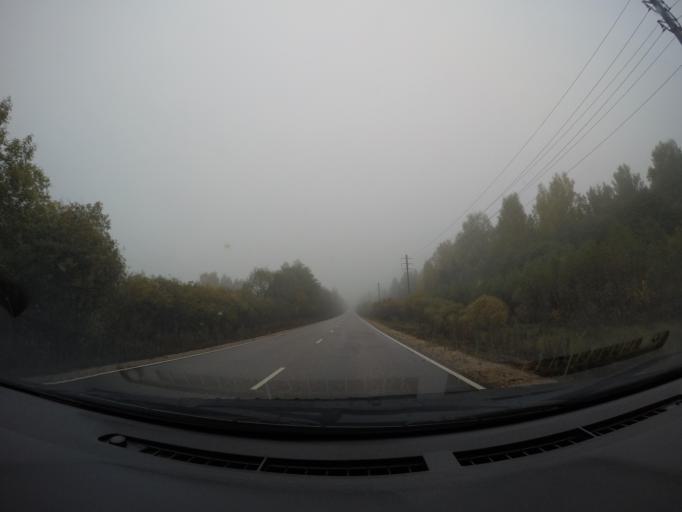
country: RU
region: Moskovskaya
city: Ruza
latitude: 55.7758
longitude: 36.2593
